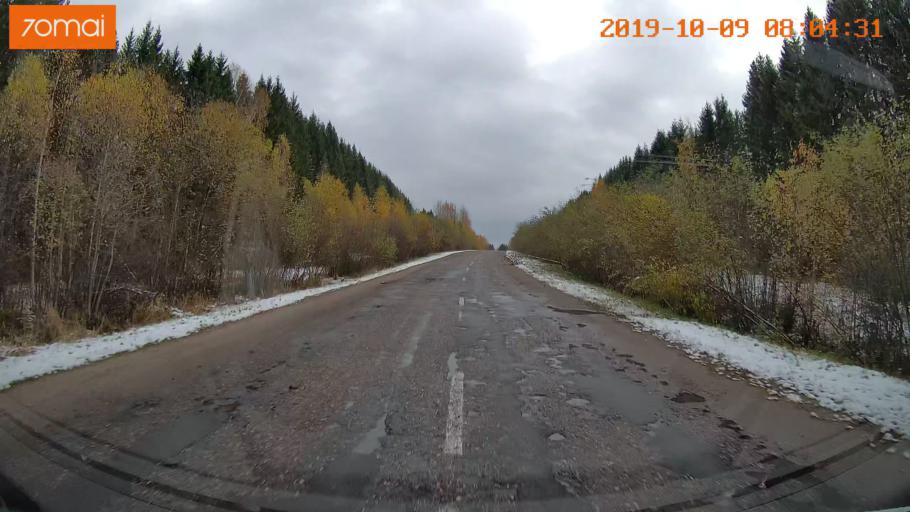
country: RU
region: Jaroslavl
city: Kukoboy
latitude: 58.6915
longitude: 40.0281
